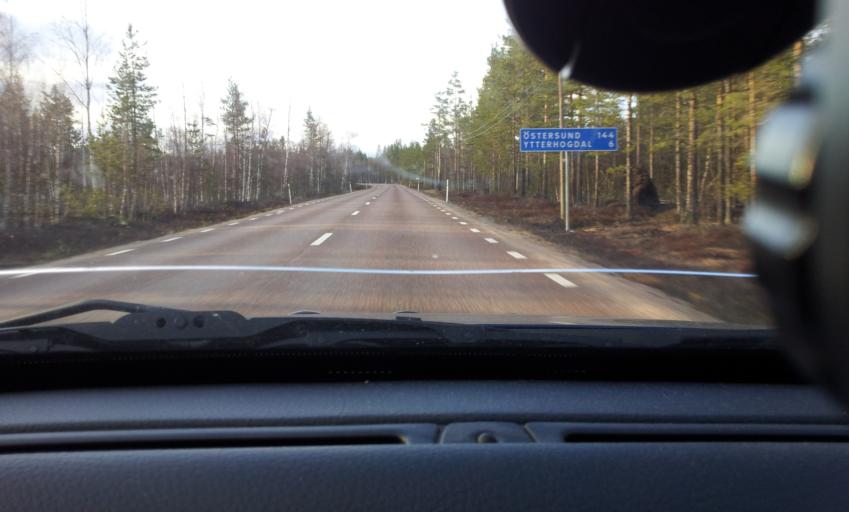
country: SE
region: Jaemtland
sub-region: Harjedalens Kommun
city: Sveg
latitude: 62.1319
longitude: 14.9714
